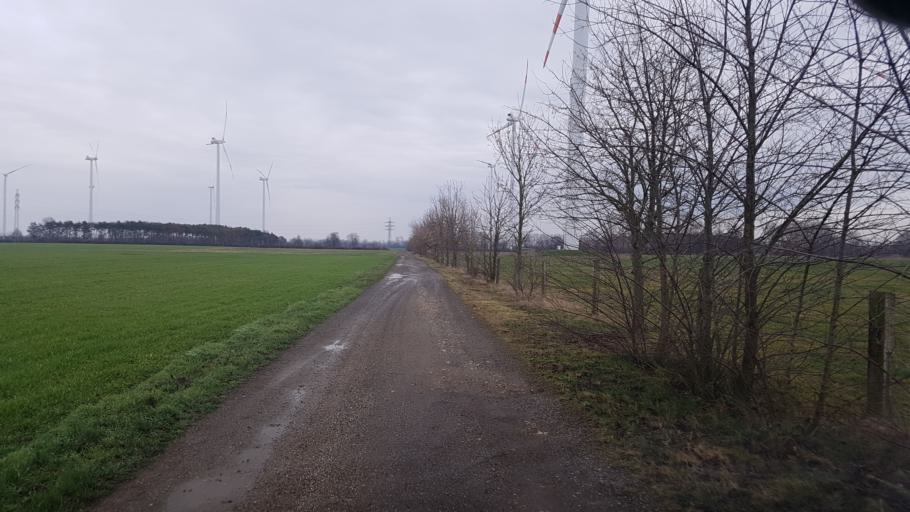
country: DE
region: Brandenburg
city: Bad Liebenwerda
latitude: 51.5213
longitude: 13.3171
